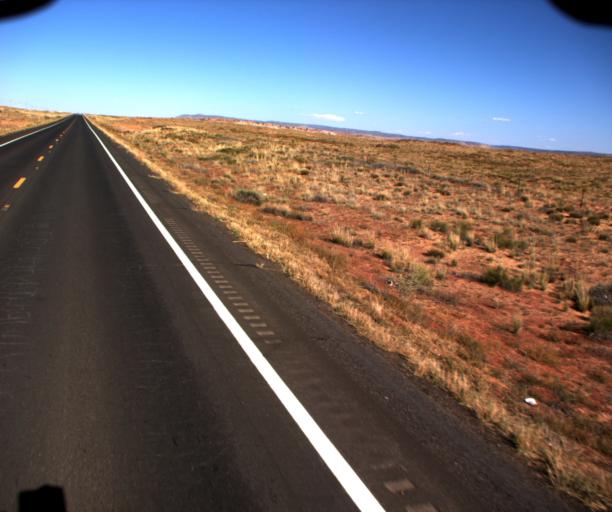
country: US
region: Arizona
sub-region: Coconino County
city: Tuba City
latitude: 36.2735
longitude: -111.0120
